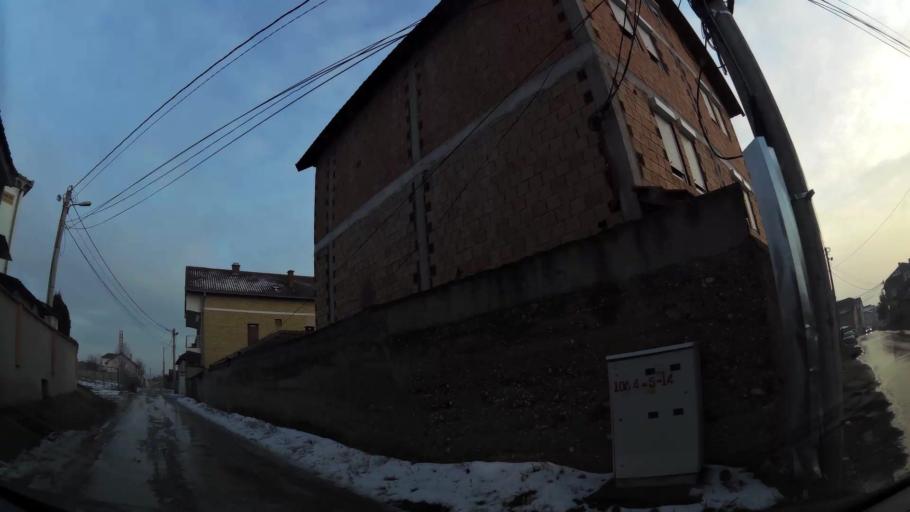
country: MK
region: Aracinovo
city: Arachinovo
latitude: 42.0301
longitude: 21.5655
